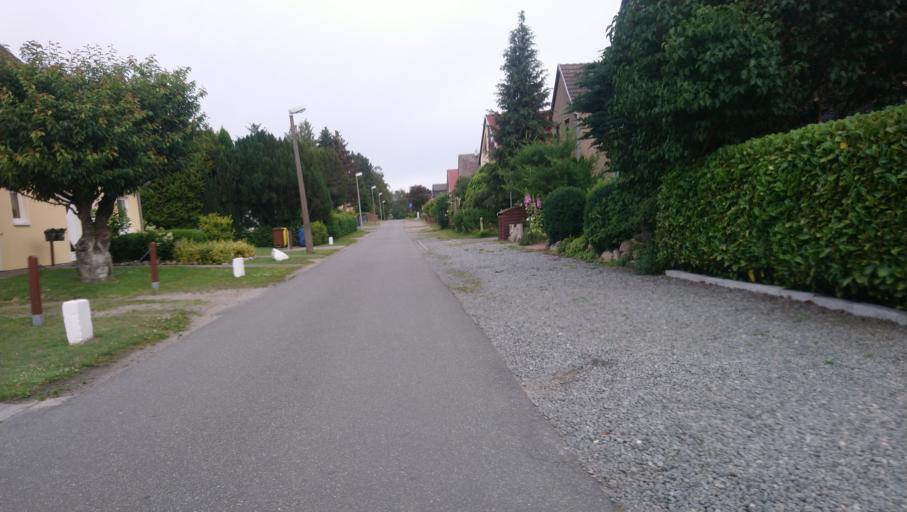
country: DE
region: Mecklenburg-Vorpommern
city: Papendorf
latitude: 54.0665
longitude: 12.1056
